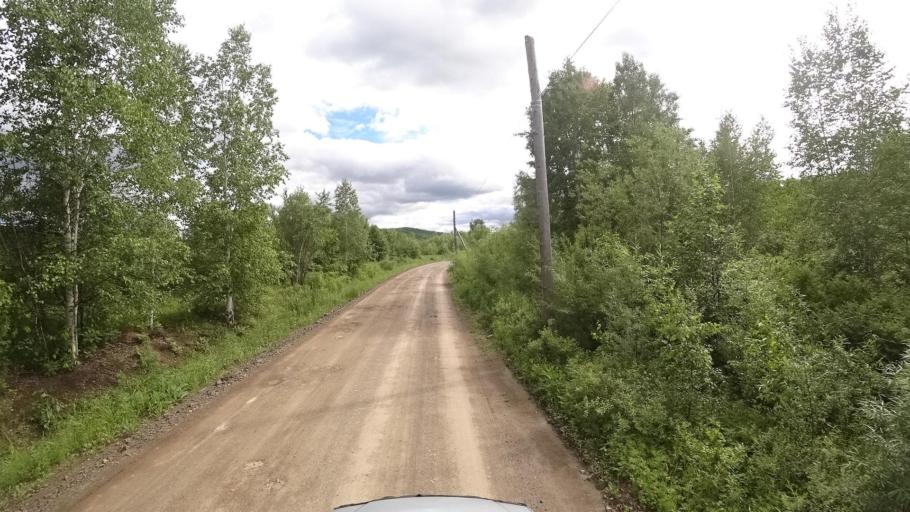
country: RU
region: Khabarovsk Krai
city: Litovko
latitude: 49.3718
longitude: 135.1730
